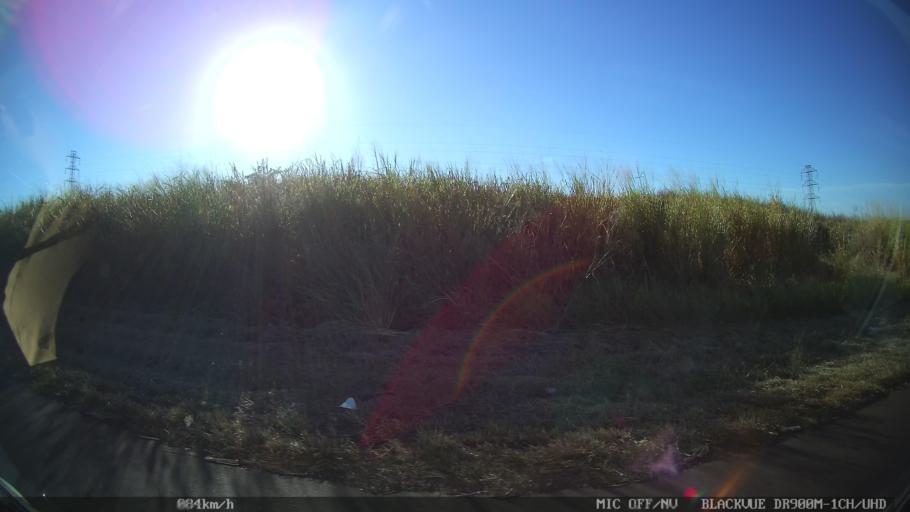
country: BR
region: Sao Paulo
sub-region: Olimpia
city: Olimpia
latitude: -20.6957
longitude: -48.9283
